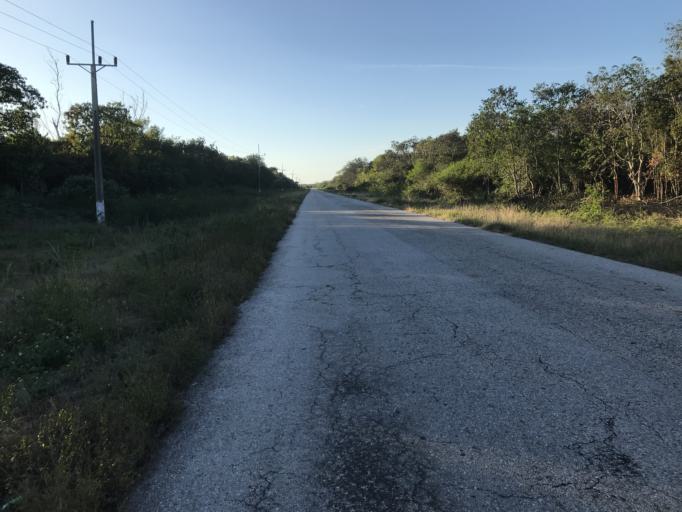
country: CU
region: Cienfuegos
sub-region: Municipio de Aguada de Pasajeros
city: Aguada de Pasajeros
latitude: 22.0770
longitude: -81.0645
